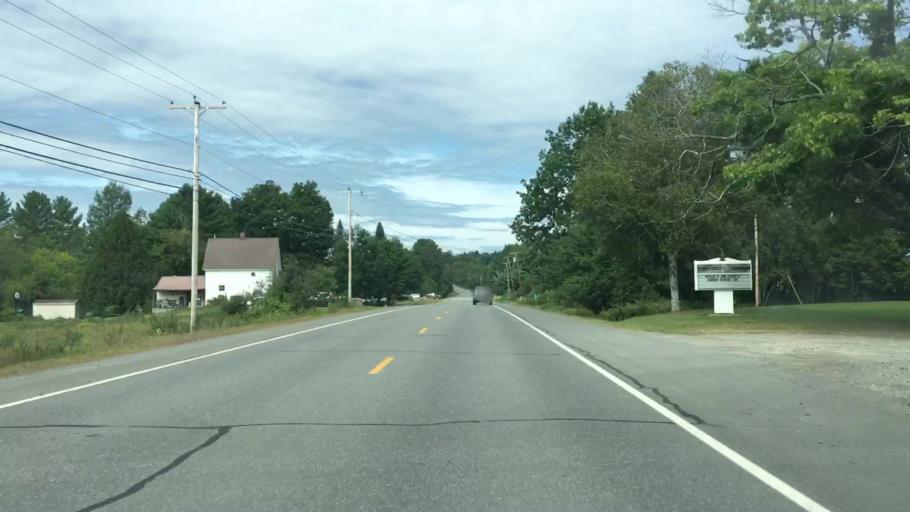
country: US
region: Maine
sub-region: Piscataquis County
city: Milo
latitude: 45.2722
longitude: -68.9999
